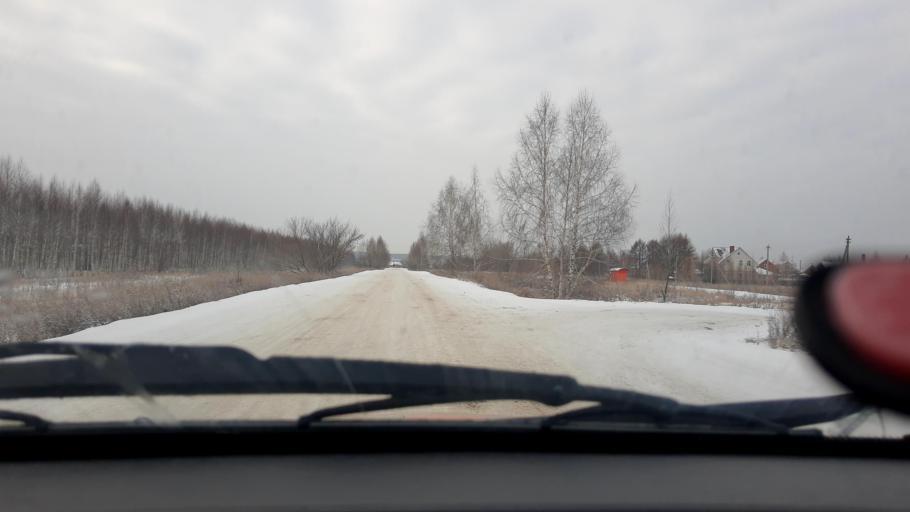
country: RU
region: Bashkortostan
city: Iglino
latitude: 54.7504
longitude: 56.2841
